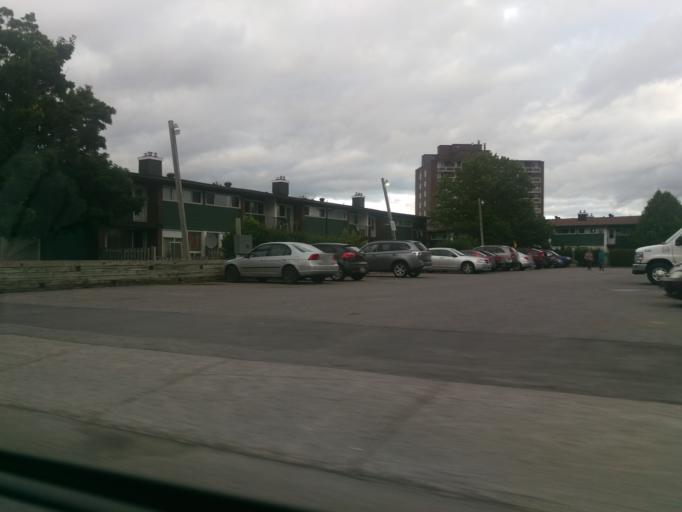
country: CA
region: Quebec
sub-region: Outaouais
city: Gatineau
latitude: 45.4579
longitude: -75.7422
